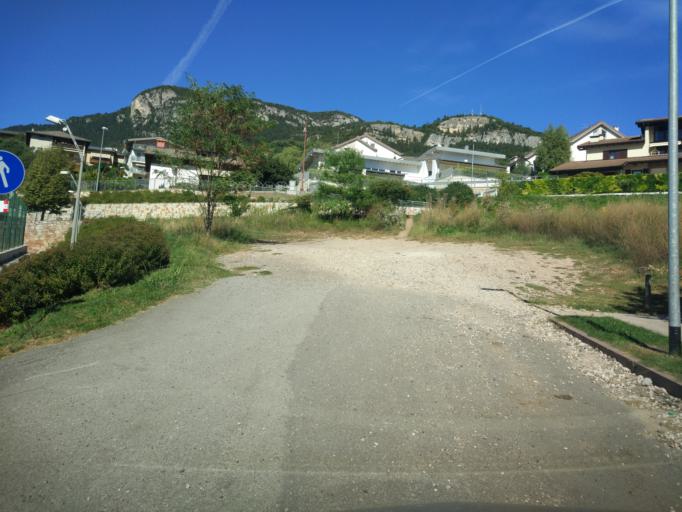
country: IT
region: Trentino-Alto Adige
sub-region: Provincia di Trento
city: Povo
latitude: 46.0779
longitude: 11.1423
